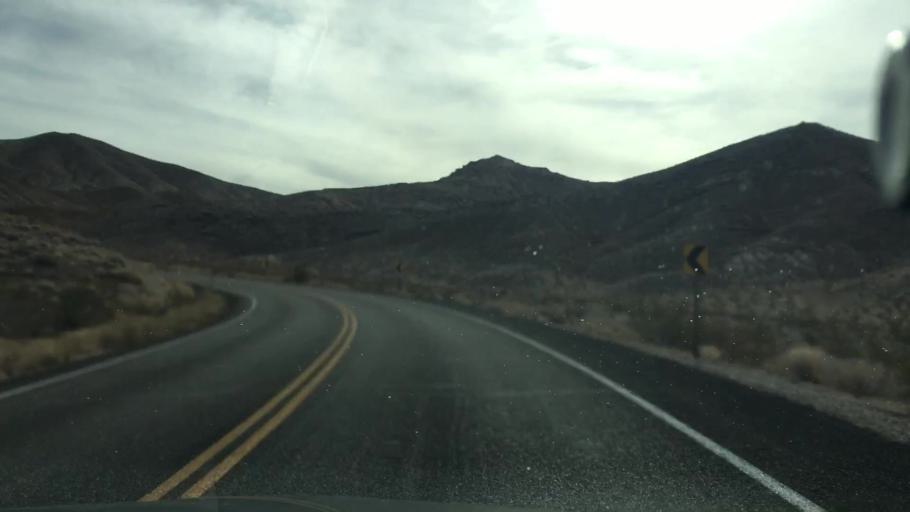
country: US
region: Nevada
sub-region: Nye County
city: Beatty
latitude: 36.7462
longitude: -116.9484
